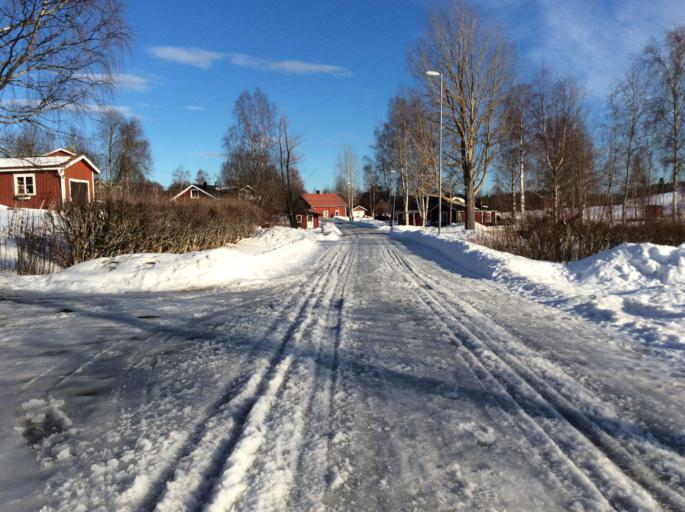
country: SE
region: Vaesterbotten
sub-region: Umea Kommun
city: Roback
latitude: 64.0378
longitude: 20.0741
